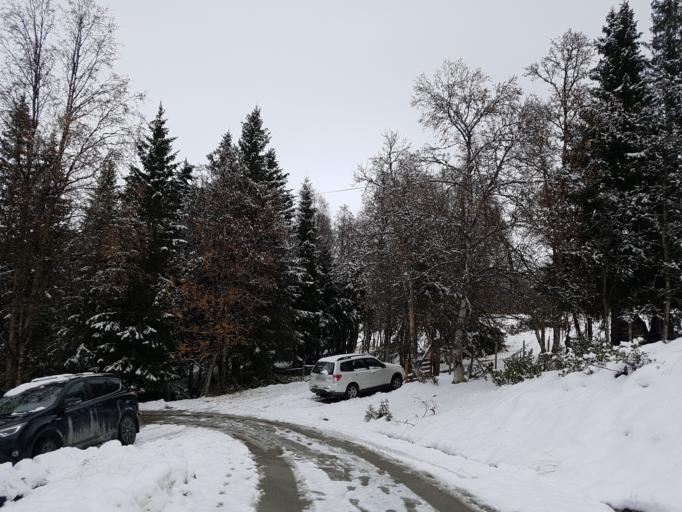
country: NO
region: Oppland
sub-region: Sel
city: Otta
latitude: 61.8075
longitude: 9.6766
